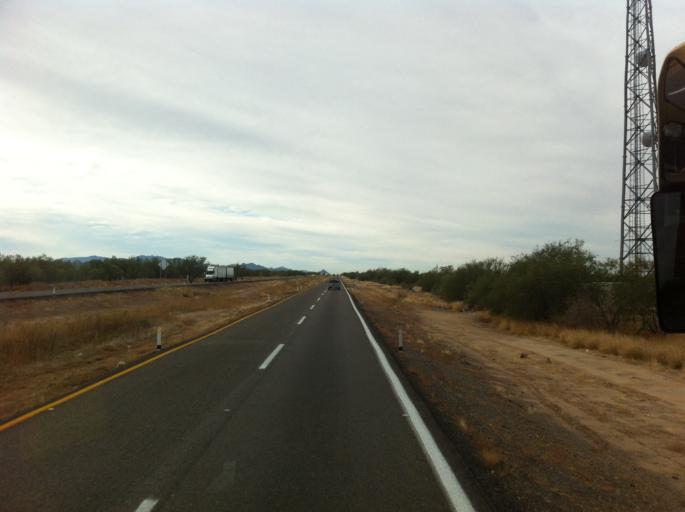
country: MX
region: Sonora
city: Hermosillo
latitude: 28.8009
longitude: -110.9587
